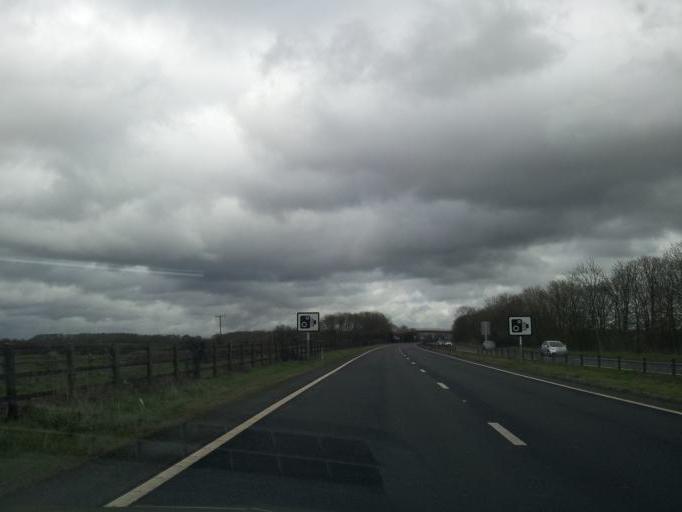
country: GB
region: England
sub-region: Somerset
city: Ilchester
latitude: 51.0245
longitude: -2.6530
